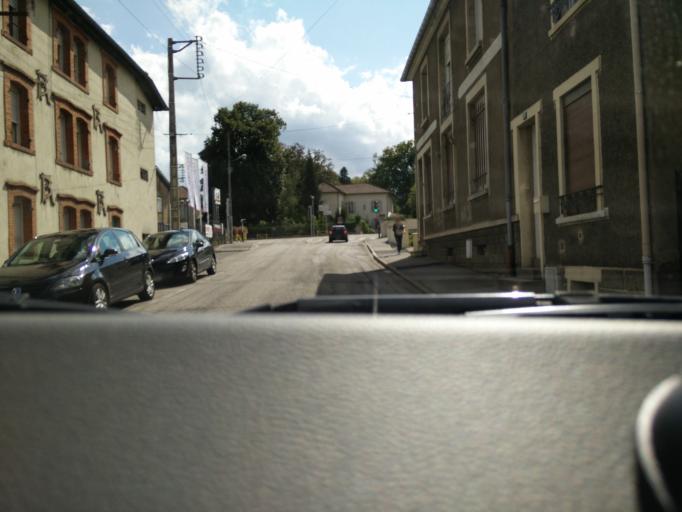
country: FR
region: Lorraine
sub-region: Departement de Meurthe-et-Moselle
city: Damelevieres
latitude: 48.5565
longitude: 6.4014
